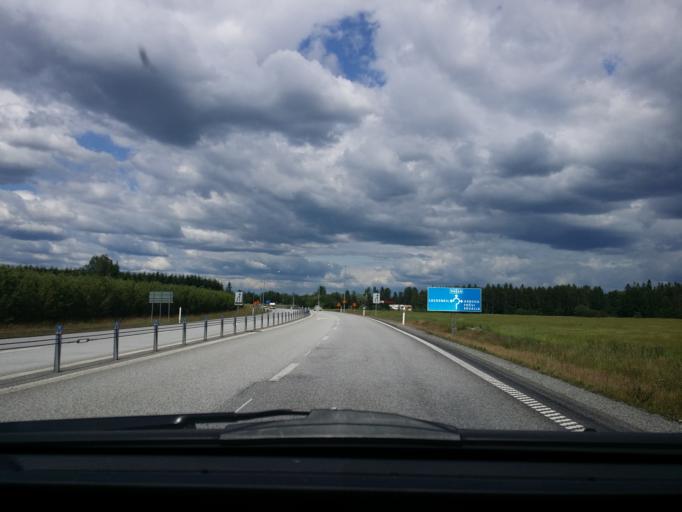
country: SE
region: OErebro
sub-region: Orebro Kommun
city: Hovsta
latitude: 59.4200
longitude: 15.1788
